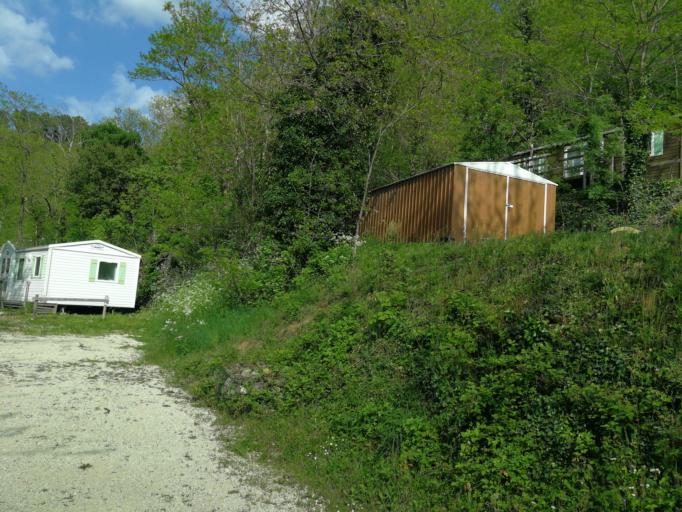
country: FR
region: Rhone-Alpes
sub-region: Departement de l'Ardeche
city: Saint-Sauveur-de-Montagut
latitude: 44.8074
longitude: 4.6153
